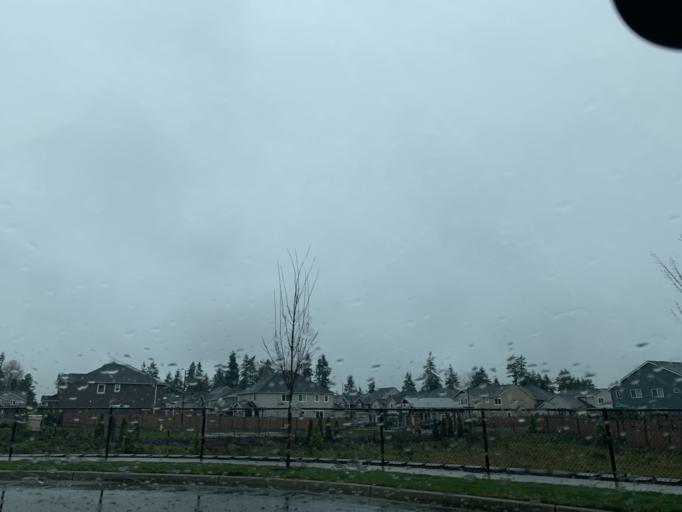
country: US
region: Washington
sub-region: King County
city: Kingsgate
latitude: 47.7390
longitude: -122.1713
